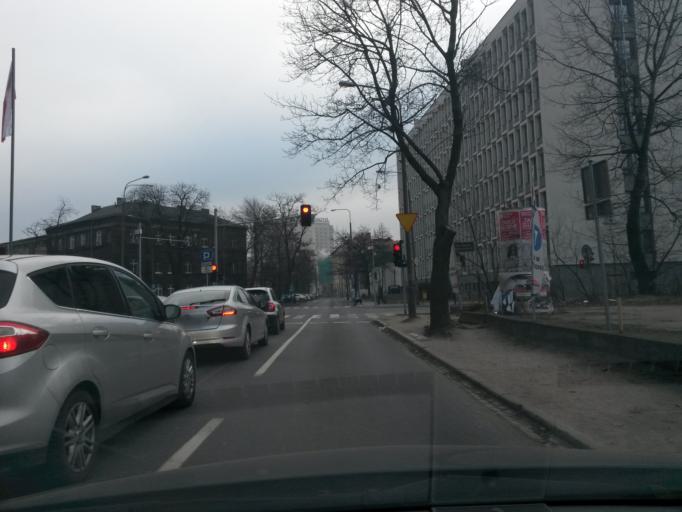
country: PL
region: Greater Poland Voivodeship
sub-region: Poznan
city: Poznan
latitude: 52.4047
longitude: 16.9211
